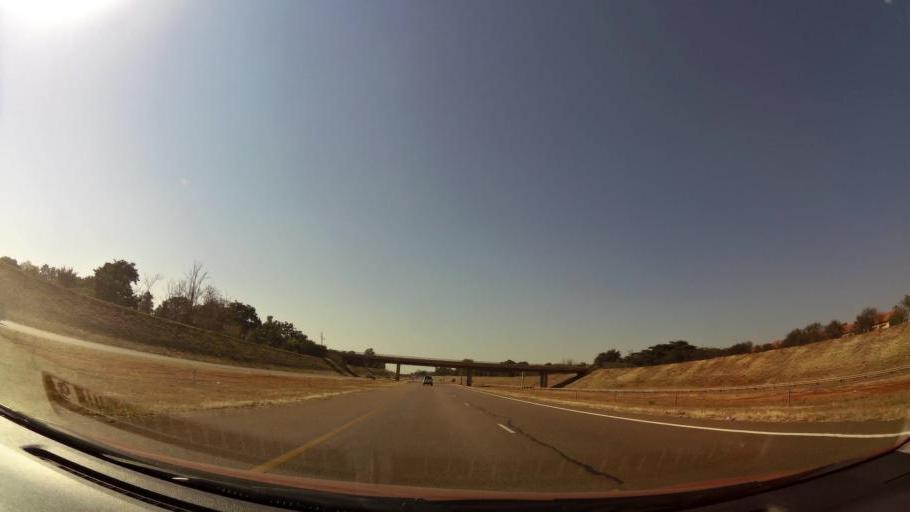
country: ZA
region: Gauteng
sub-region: City of Tshwane Metropolitan Municipality
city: Pretoria
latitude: -25.6538
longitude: 28.1225
